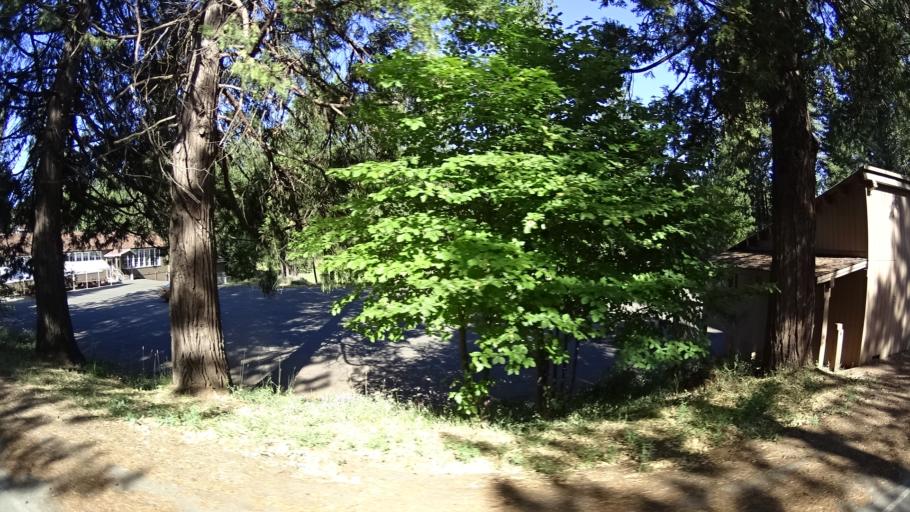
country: US
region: California
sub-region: Calaveras County
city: Arnold
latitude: 38.2631
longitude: -120.3418
